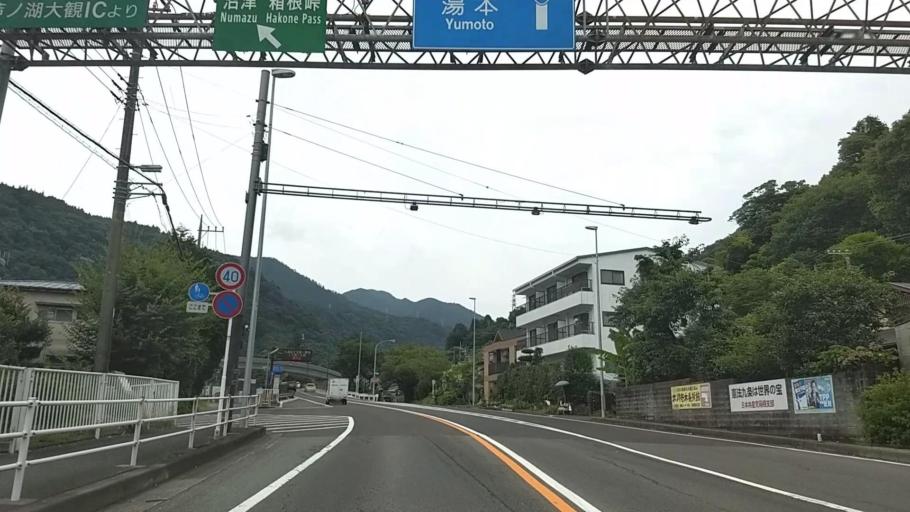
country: JP
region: Kanagawa
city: Odawara
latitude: 35.2370
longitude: 139.1159
